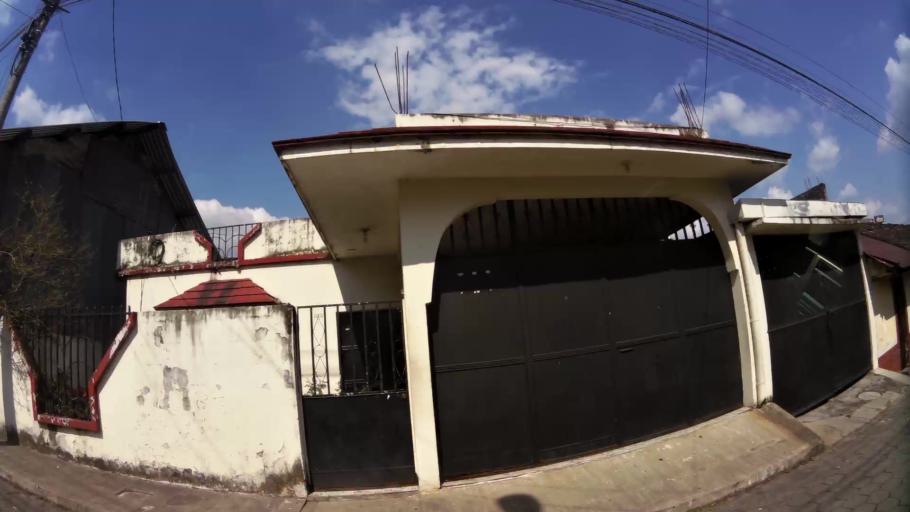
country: GT
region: Suchitepeque
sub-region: Municipio de Cuyotenango
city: Cuyotenango
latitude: 14.5404
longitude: -91.5733
